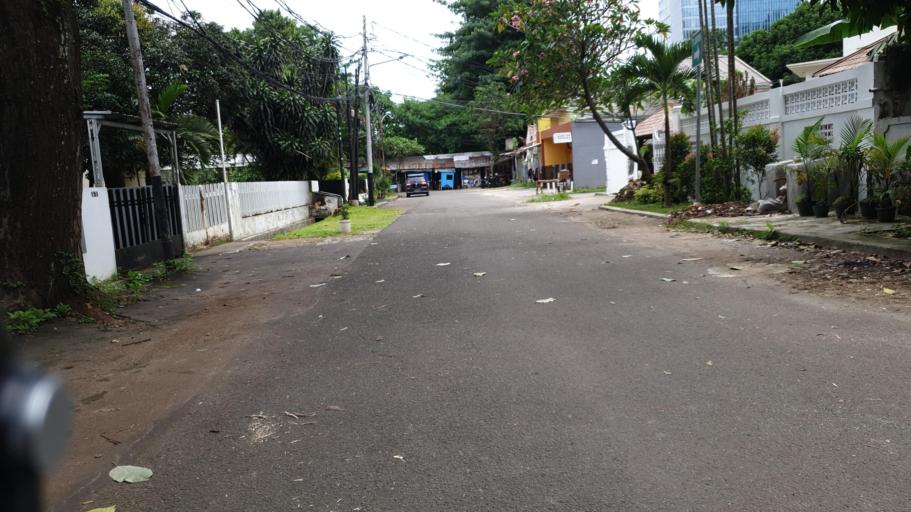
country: ID
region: Banten
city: South Tangerang
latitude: -6.2927
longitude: 106.7809
